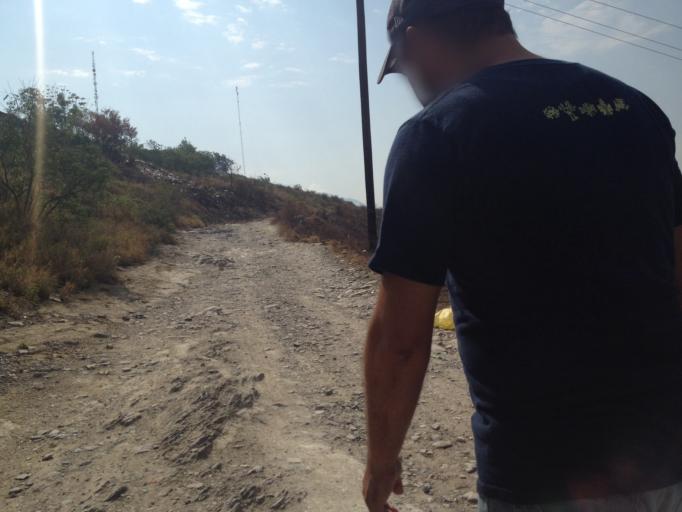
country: MX
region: Nuevo Leon
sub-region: Monterrey
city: Monterrey
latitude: 25.6543
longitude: -100.3309
